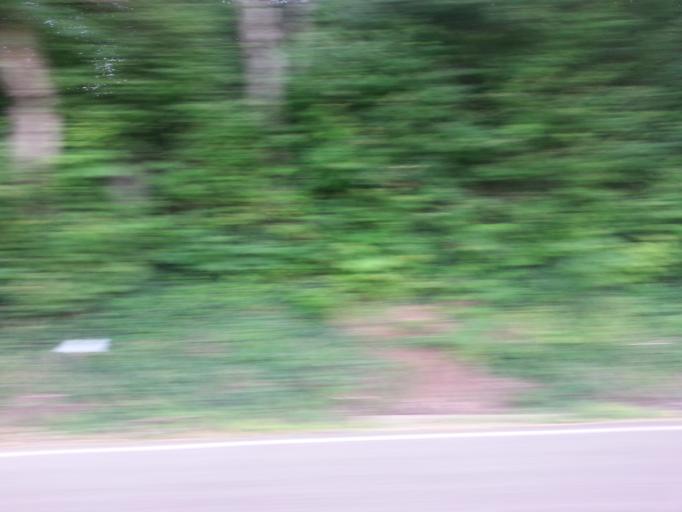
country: US
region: Tennessee
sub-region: Knox County
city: Knoxville
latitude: 36.0167
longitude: -83.8573
